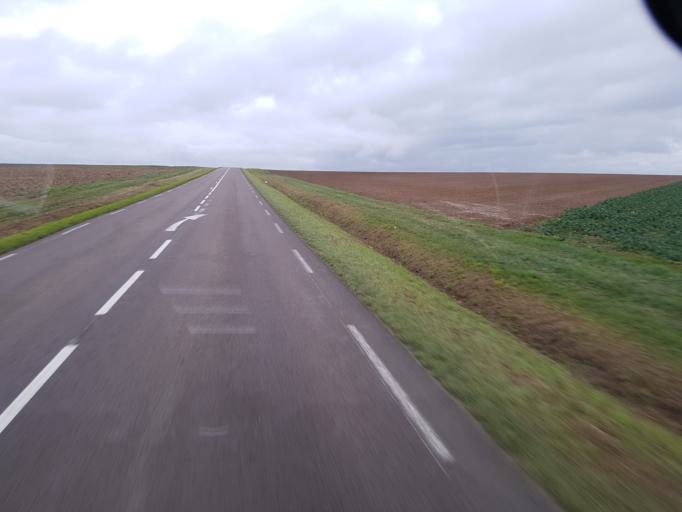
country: FR
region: Champagne-Ardenne
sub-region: Departement de la Marne
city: Sezanne
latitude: 48.7402
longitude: 3.6753
